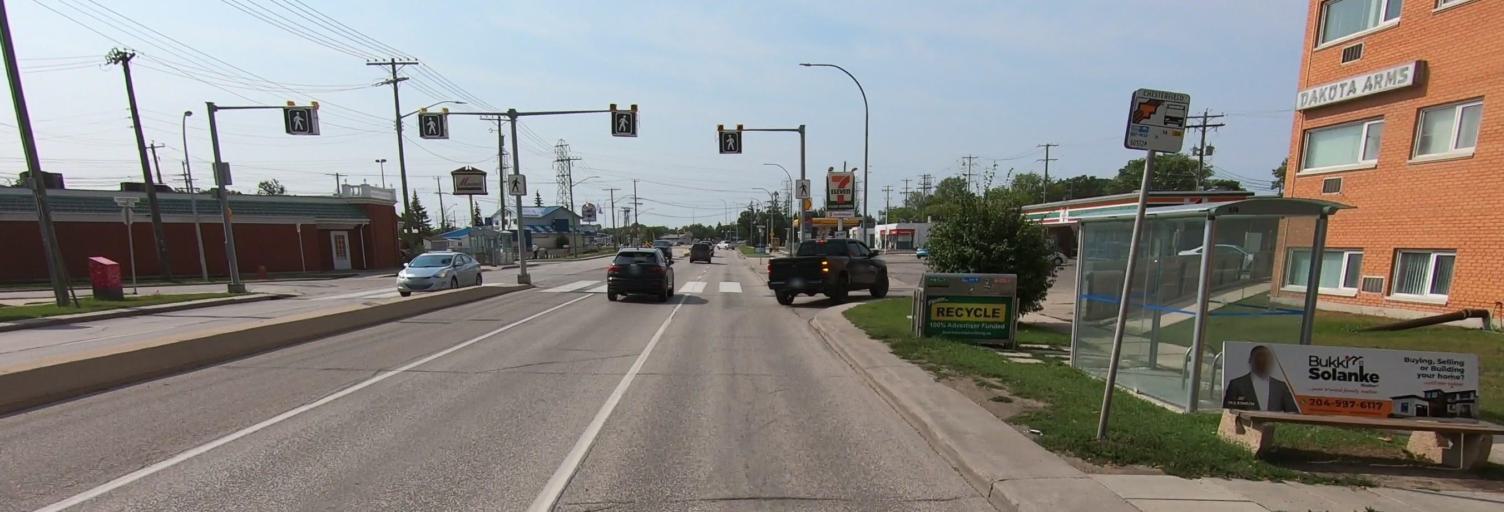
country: CA
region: Manitoba
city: Winnipeg
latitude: 49.8339
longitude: -97.1141
